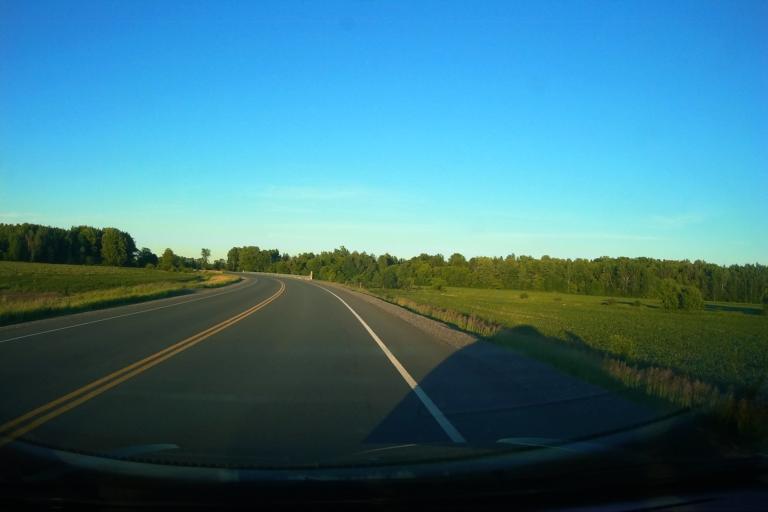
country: CA
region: Ontario
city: Casselman
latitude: 45.0720
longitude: -75.3611
